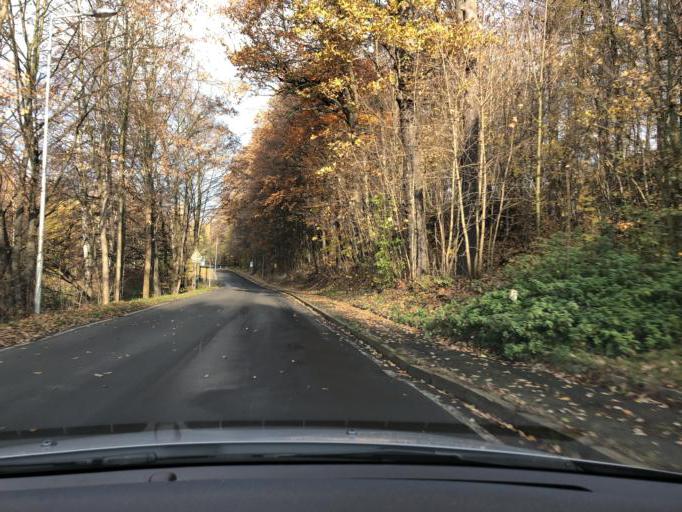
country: DE
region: Saxony
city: Nerchau
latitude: 51.2492
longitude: 12.7757
